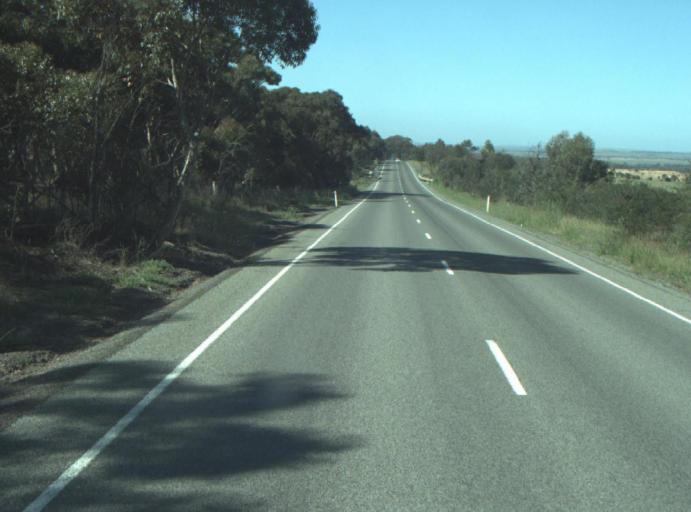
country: AU
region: Victoria
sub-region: Greater Geelong
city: Lara
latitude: -37.9098
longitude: 144.3986
